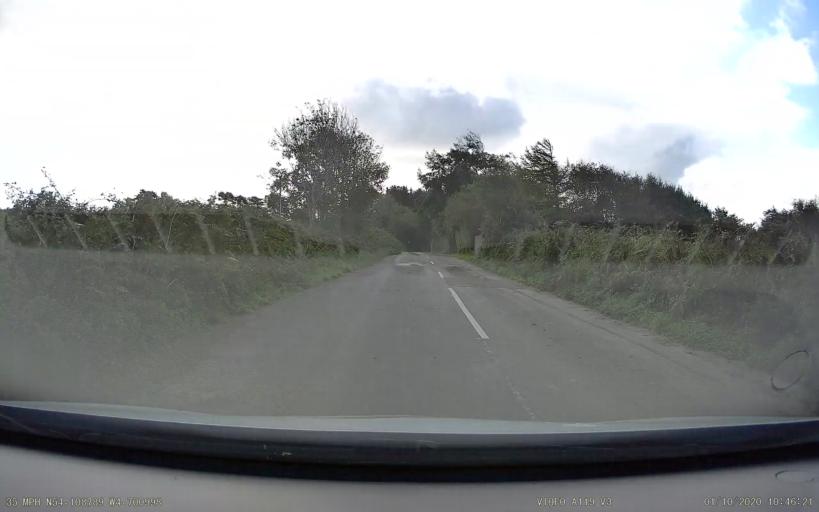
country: IM
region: Port Erin
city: Port Erin
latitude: 54.1088
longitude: -4.7010
